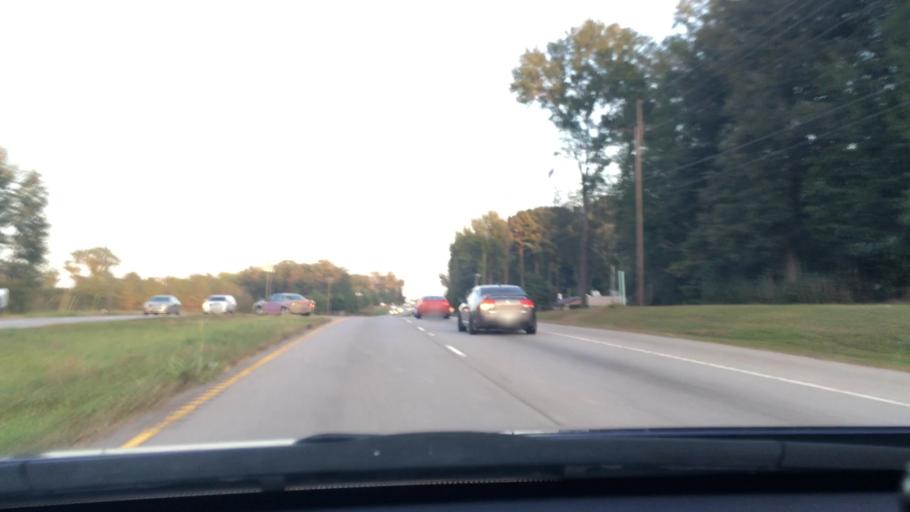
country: US
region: South Carolina
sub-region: Richland County
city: Hopkins
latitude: 33.9444
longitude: -80.8927
